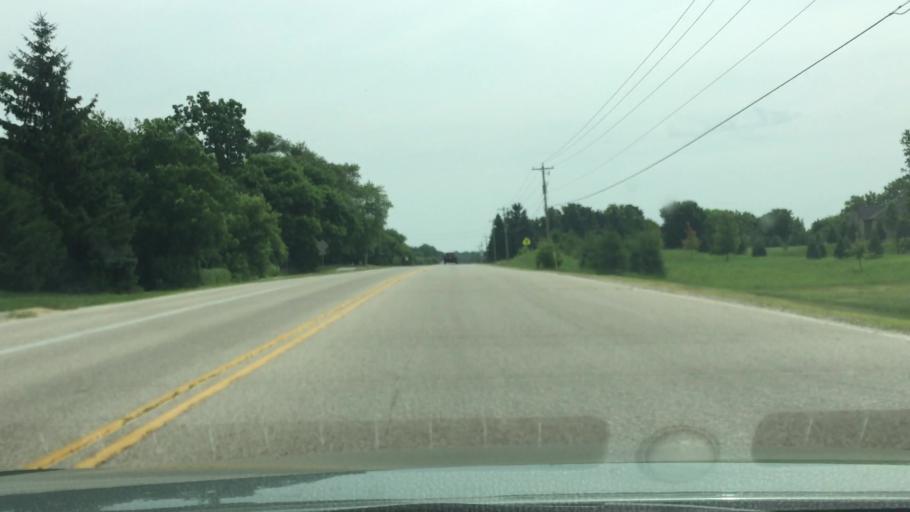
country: US
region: Wisconsin
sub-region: Waukesha County
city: Hartland
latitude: 43.0829
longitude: -88.3397
